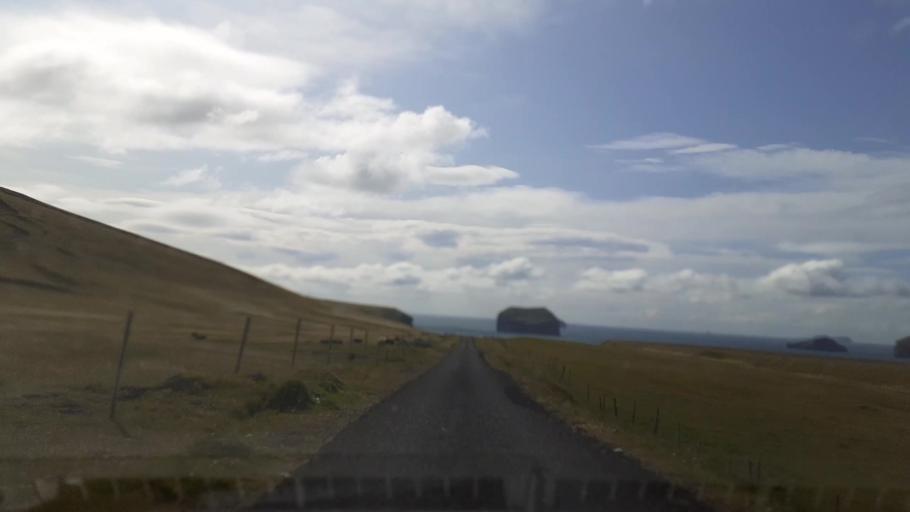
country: IS
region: South
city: Vestmannaeyjar
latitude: 63.4231
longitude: -20.2771
